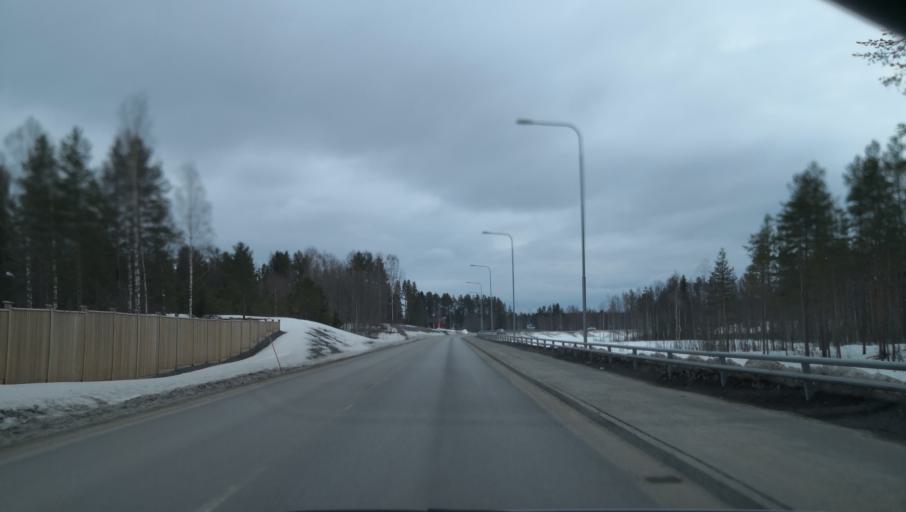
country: SE
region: Vaesterbotten
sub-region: Vannas Kommun
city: Vaennaes
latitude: 63.9109
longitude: 19.7698
